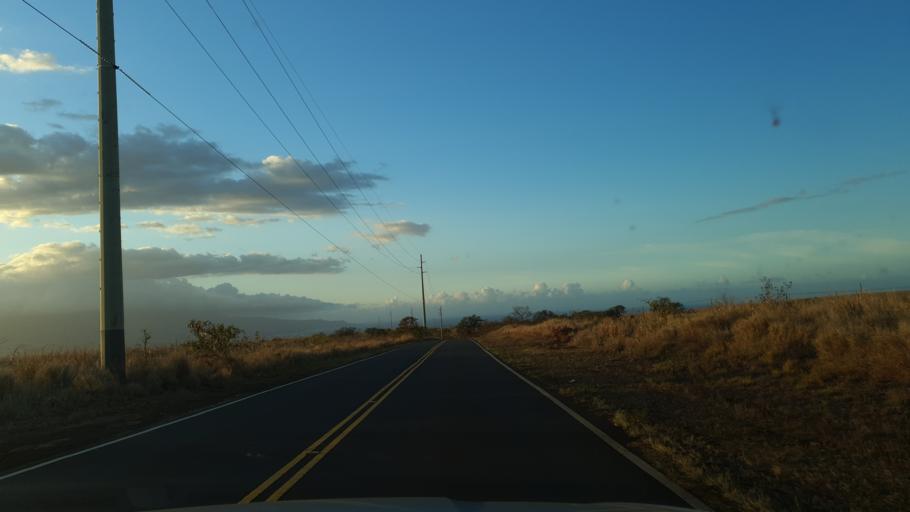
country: US
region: Hawaii
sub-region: Maui County
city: Pukalani
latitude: 20.8107
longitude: -156.3821
